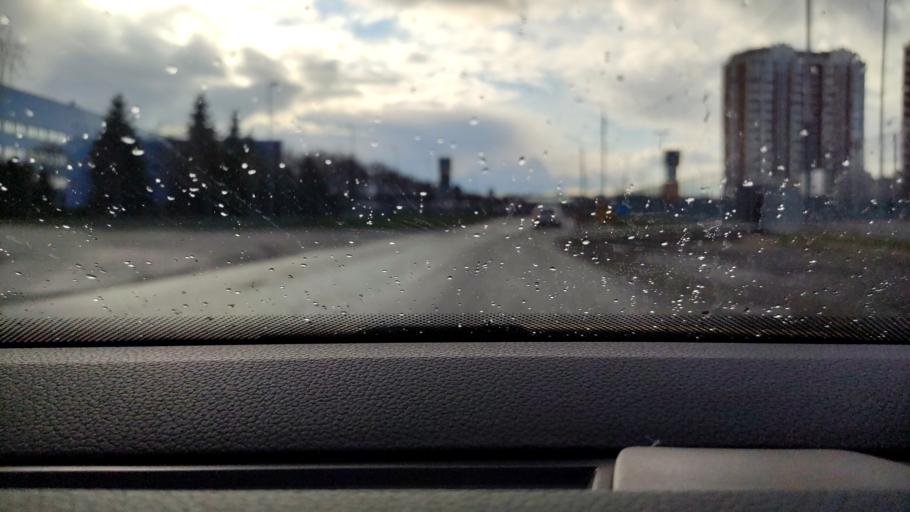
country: RU
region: Moskovskaya
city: Saltykovka
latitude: 55.7414
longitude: 37.9628
